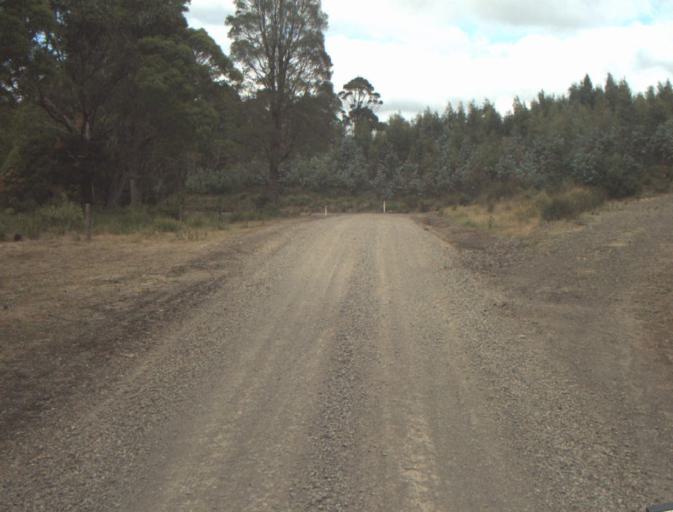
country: AU
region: Tasmania
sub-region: Northern Midlands
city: Evandale
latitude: -41.4527
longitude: 147.4766
